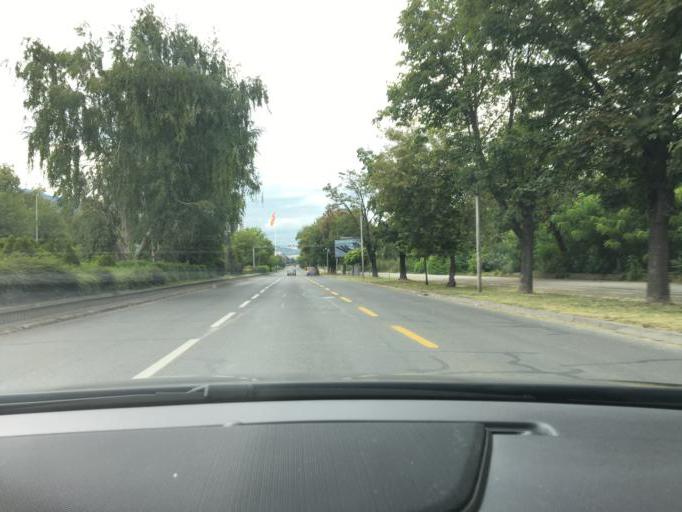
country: MK
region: Cair
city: Cair
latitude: 42.0005
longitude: 21.4575
